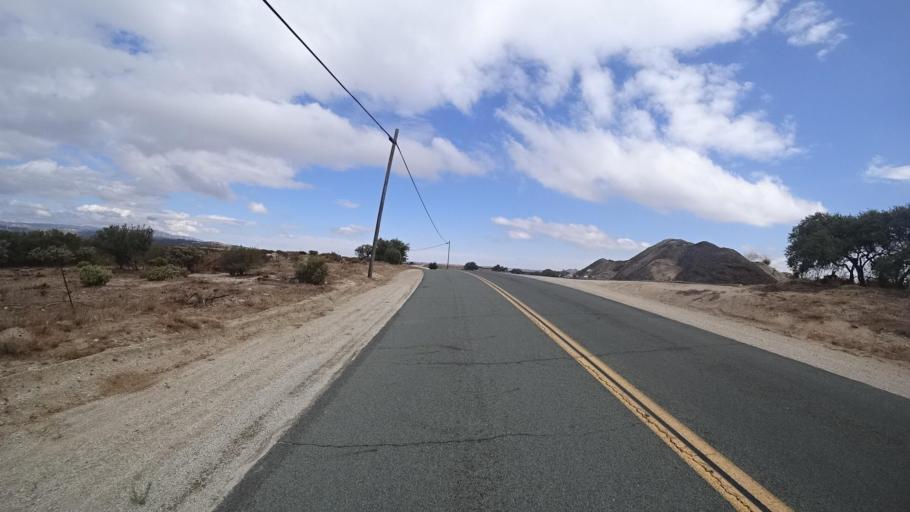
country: US
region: California
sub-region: San Diego County
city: Campo
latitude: 32.6530
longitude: -116.3154
